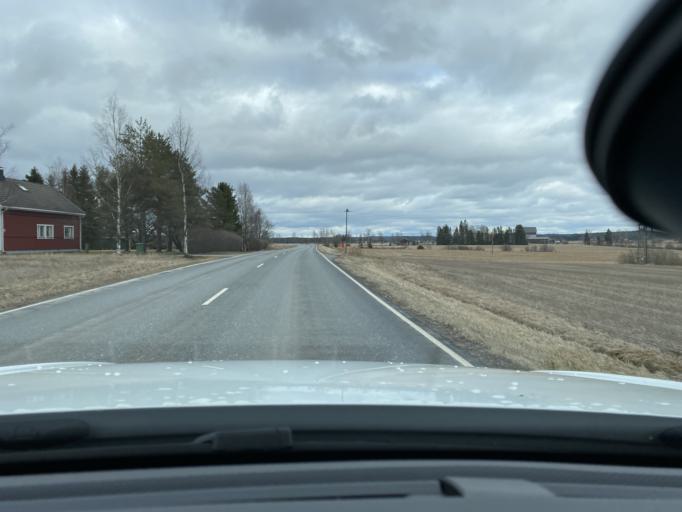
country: FI
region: Pirkanmaa
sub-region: Lounais-Pirkanmaa
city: Punkalaidun
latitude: 61.1046
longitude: 23.1461
